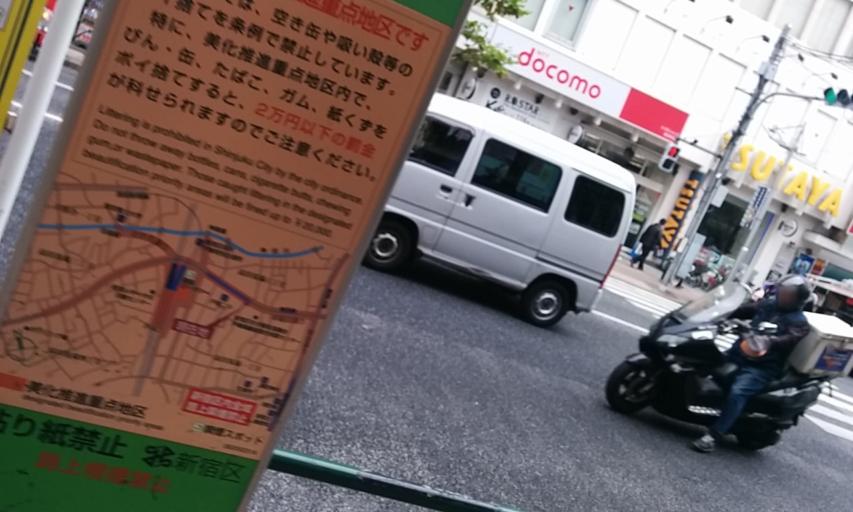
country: JP
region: Tokyo
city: Tokyo
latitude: 35.7125
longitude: 139.7070
